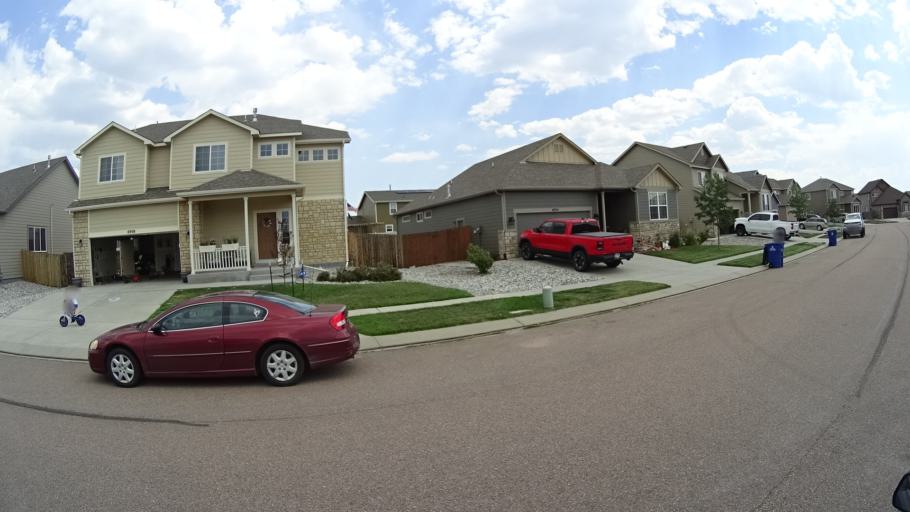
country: US
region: Colorado
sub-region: El Paso County
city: Black Forest
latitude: 38.9451
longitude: -104.6908
